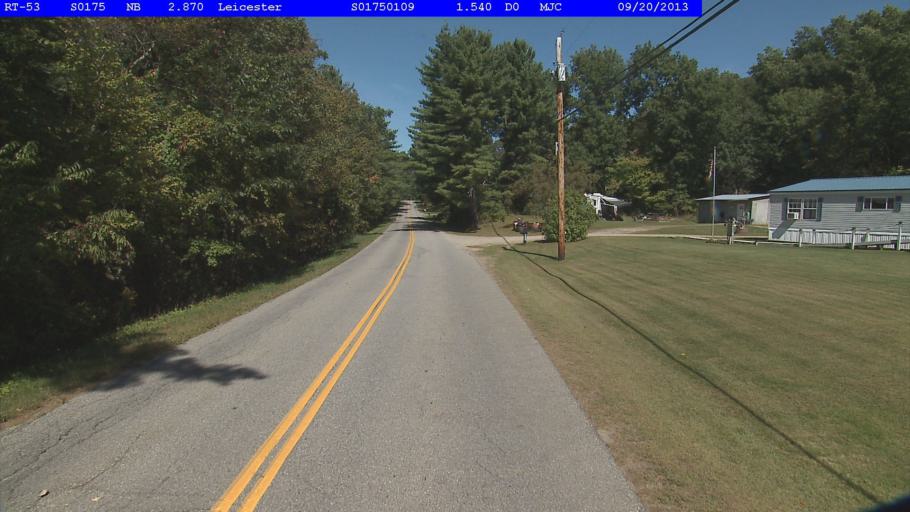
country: US
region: Vermont
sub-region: Rutland County
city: Brandon
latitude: 43.8651
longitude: -73.0660
